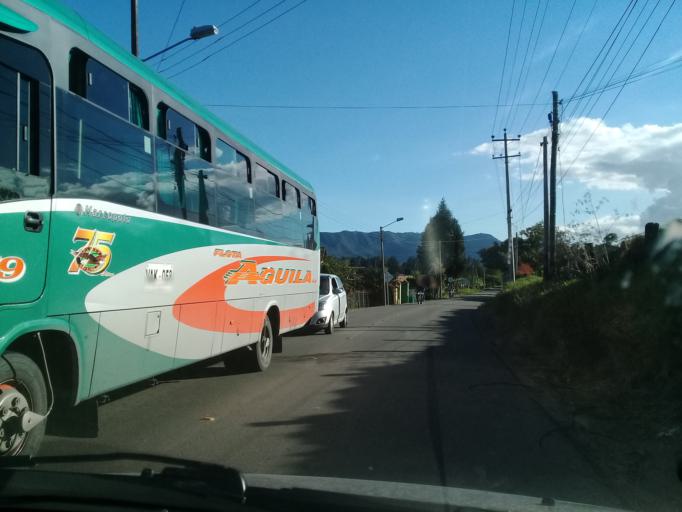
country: CO
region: Cundinamarca
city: Tabio
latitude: 4.8955
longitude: -74.1129
